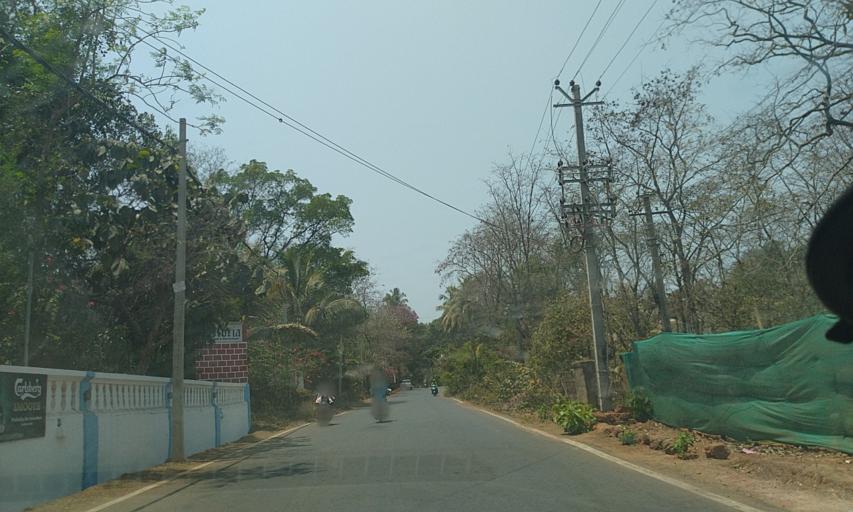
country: IN
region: Goa
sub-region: North Goa
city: Mapuca
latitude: 15.5972
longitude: 73.7893
